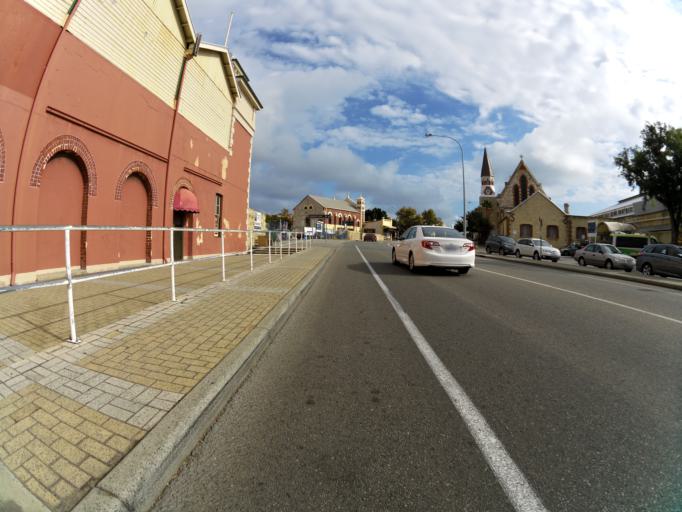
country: AU
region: Western Australia
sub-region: Fremantle
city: South Fremantle
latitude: -32.0560
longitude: 115.7500
